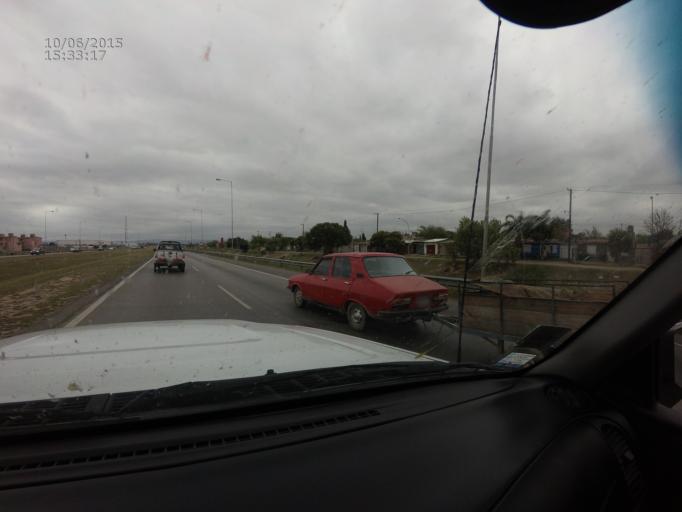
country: AR
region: Cordoba
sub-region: Departamento de Capital
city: Cordoba
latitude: -31.3605
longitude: -64.1587
